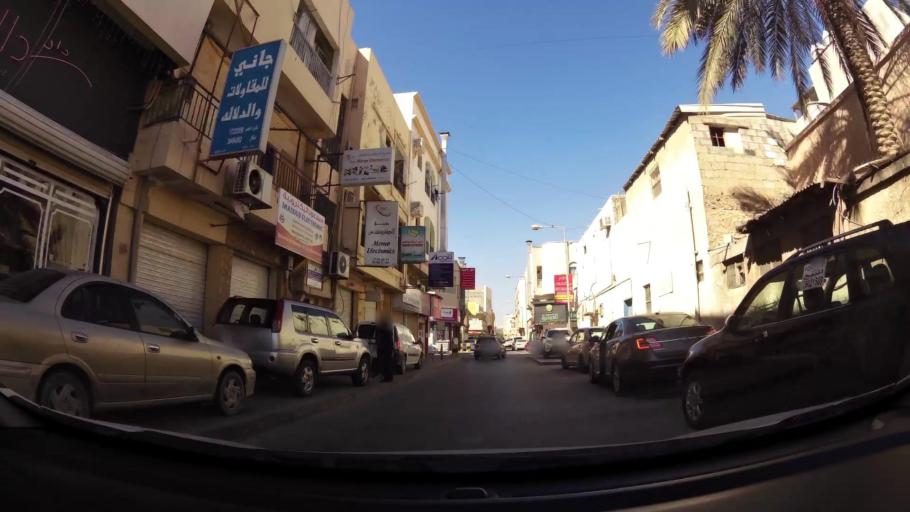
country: BH
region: Muharraq
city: Al Muharraq
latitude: 26.2608
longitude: 50.6115
